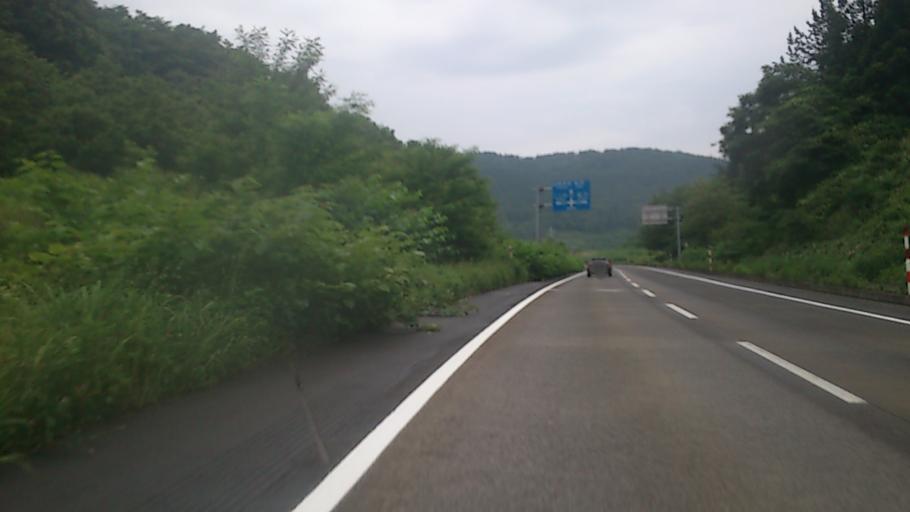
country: JP
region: Akita
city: Takanosu
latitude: 40.2158
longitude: 140.2298
